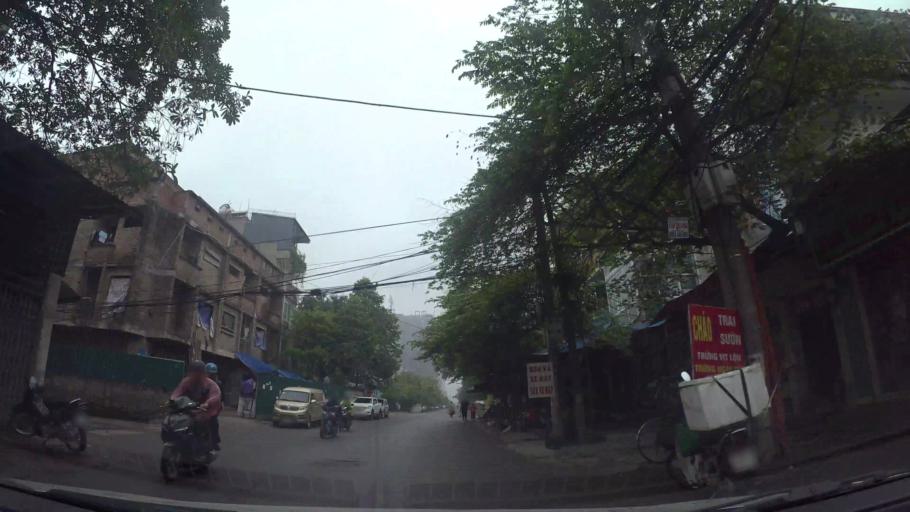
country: VN
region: Ha Noi
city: Cau Giay
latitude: 21.0219
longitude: 105.7976
